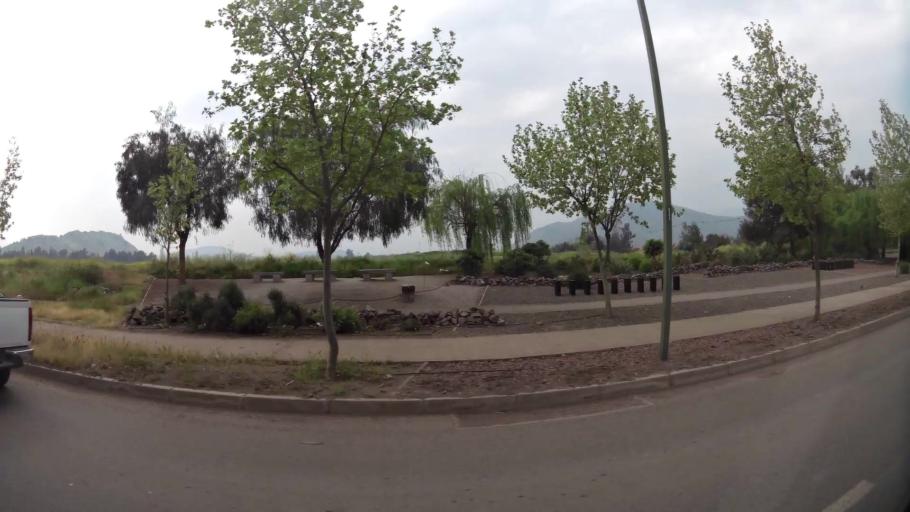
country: CL
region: Santiago Metropolitan
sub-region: Provincia de Chacabuco
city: Chicureo Abajo
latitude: -33.2014
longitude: -70.6552
